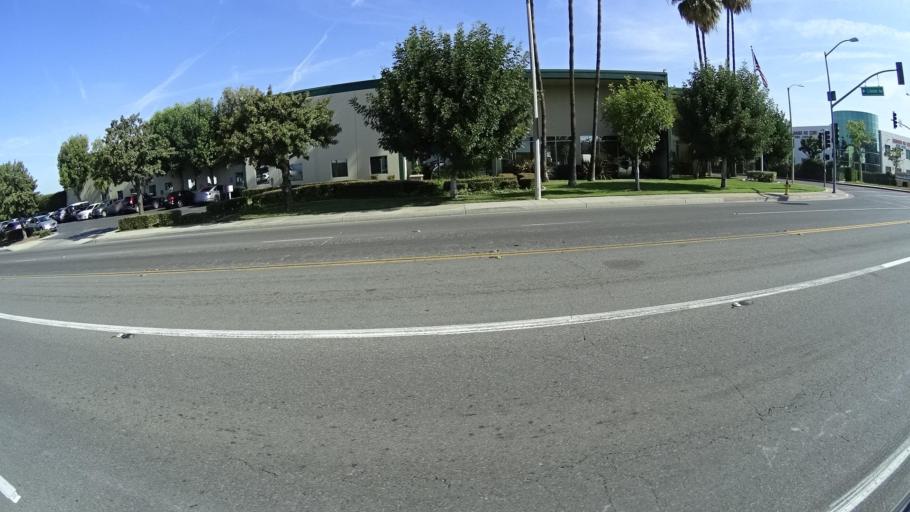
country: US
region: California
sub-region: Los Angeles County
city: South San Jose Hills
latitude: 34.0014
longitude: -117.9238
